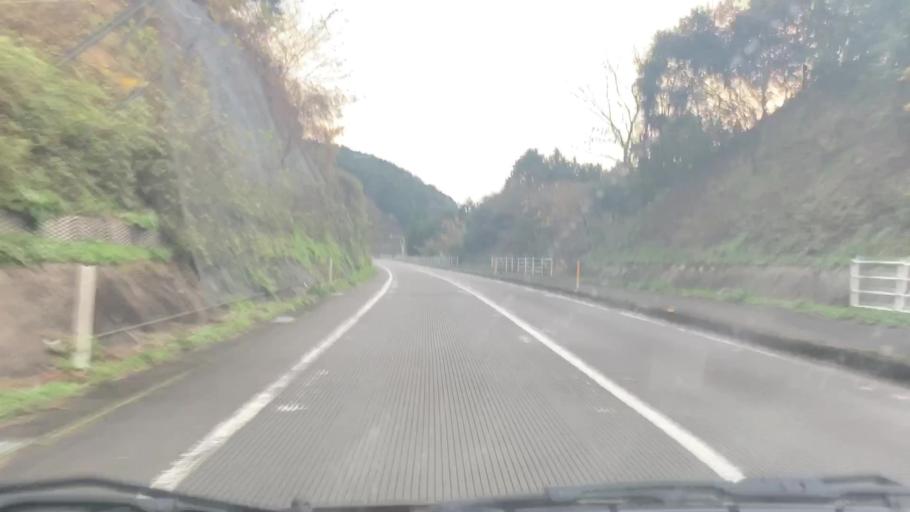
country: JP
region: Saga Prefecture
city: Kashima
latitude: 33.0449
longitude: 130.0717
